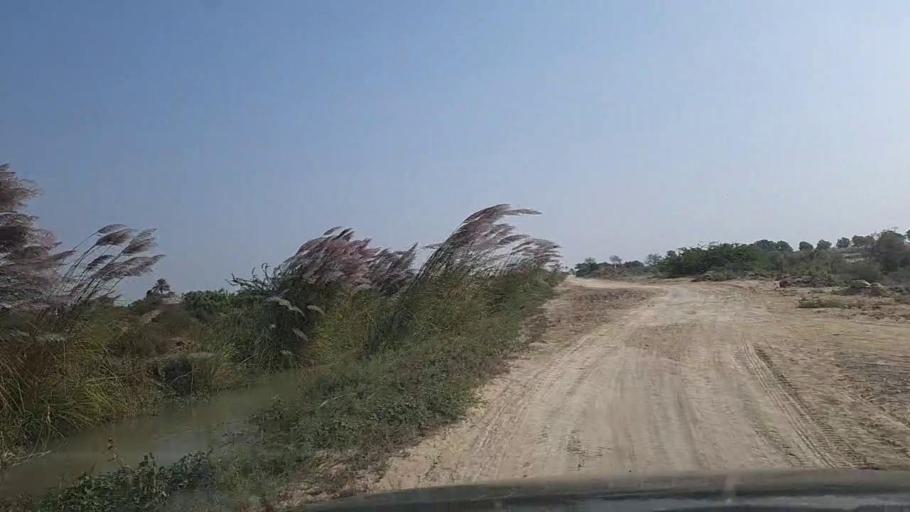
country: PK
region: Sindh
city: Gharo
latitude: 24.7163
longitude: 67.5695
